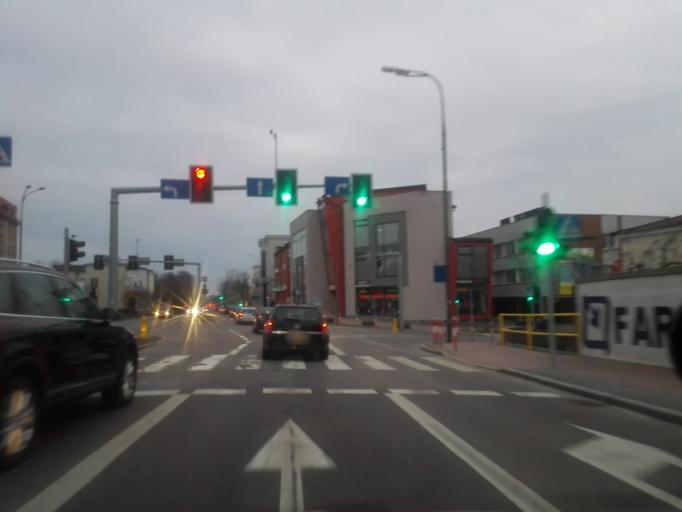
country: PL
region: Podlasie
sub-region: Lomza
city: Lomza
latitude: 53.1784
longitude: 22.0735
